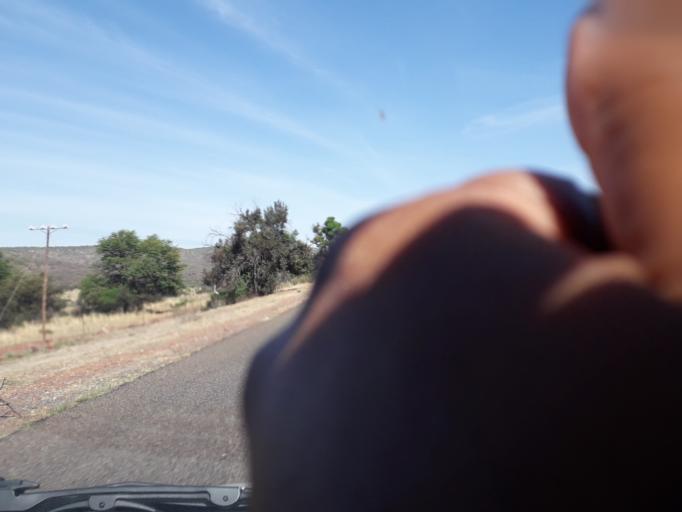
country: ZA
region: Limpopo
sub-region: Waterberg District Municipality
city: Warmbaths
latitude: -24.8297
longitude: 28.2202
